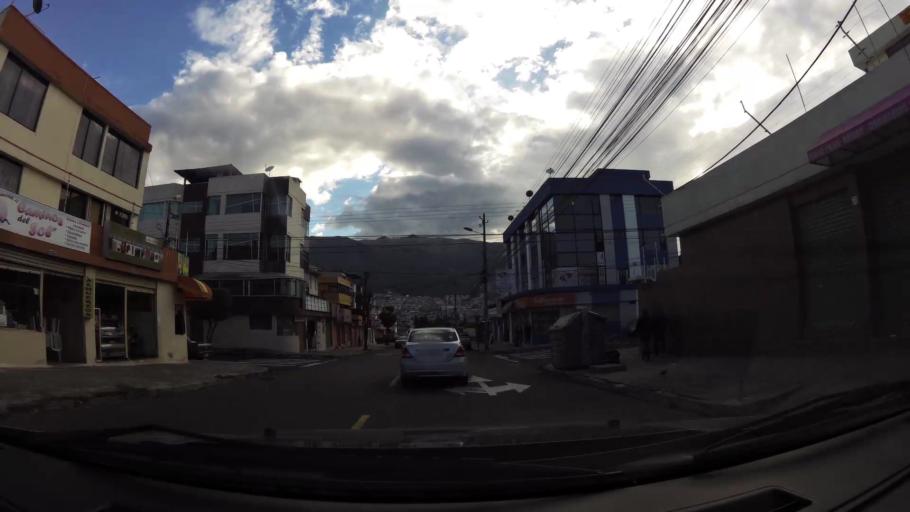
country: EC
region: Pichincha
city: Quito
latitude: -0.1410
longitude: -78.4808
